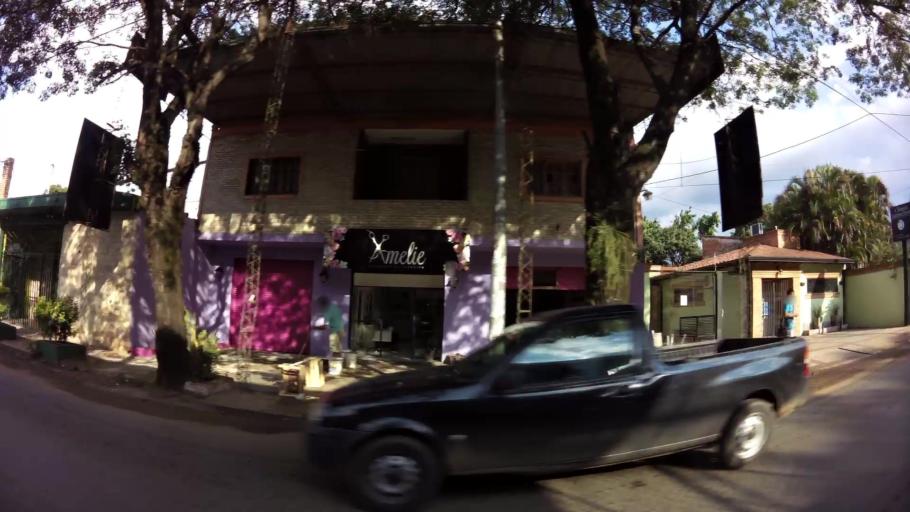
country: PY
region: Central
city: Fernando de la Mora
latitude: -25.3449
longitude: -57.5481
